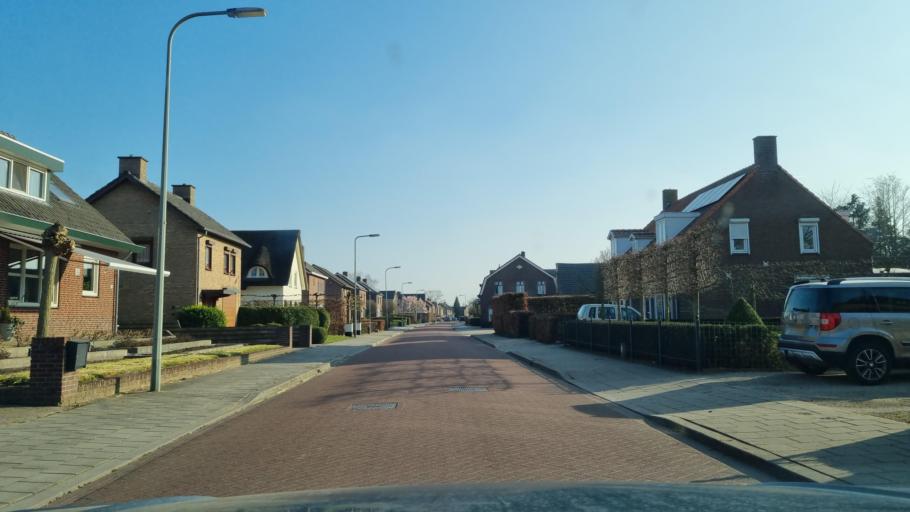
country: NL
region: Limburg
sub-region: Gemeente Gennep
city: Gennep
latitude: 51.7151
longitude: 6.0253
